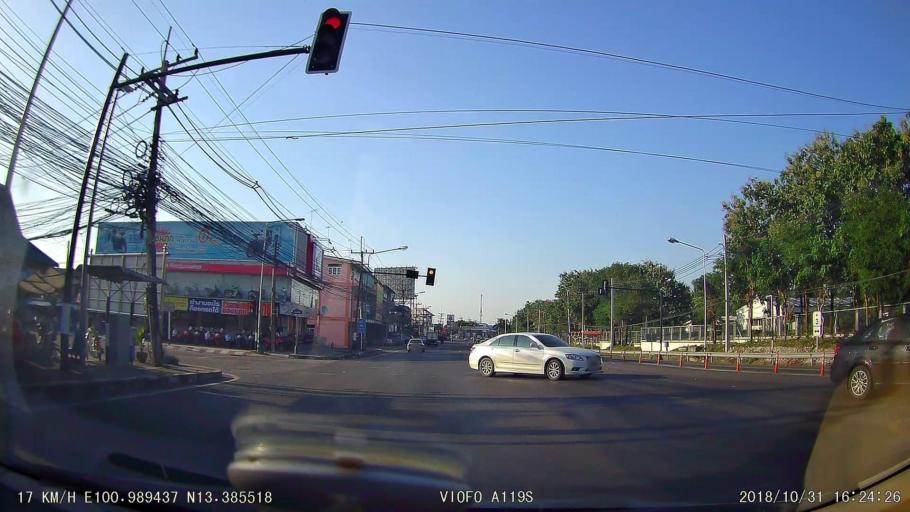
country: TH
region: Chon Buri
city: Chon Buri
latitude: 13.3855
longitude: 100.9894
